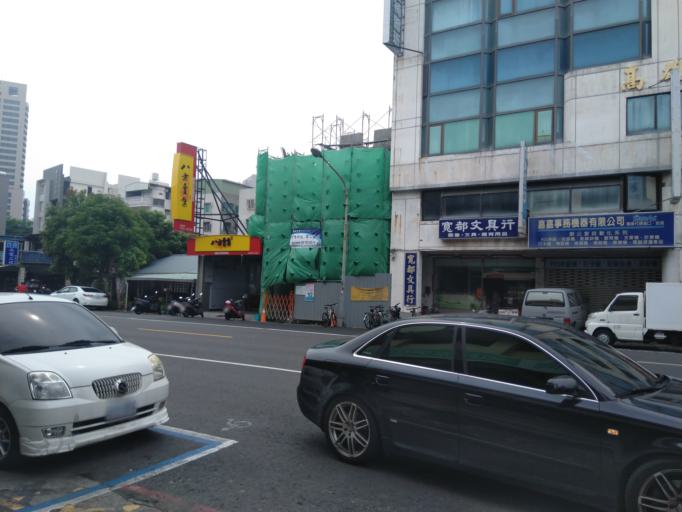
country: TW
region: Kaohsiung
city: Kaohsiung
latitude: 22.6099
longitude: 120.3101
